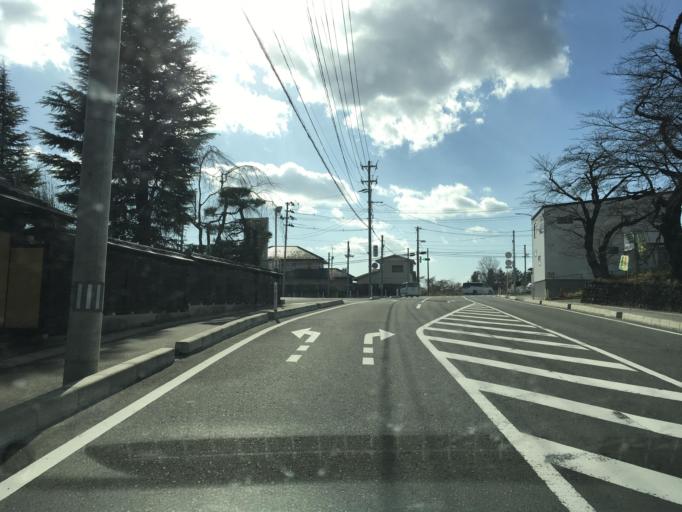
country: JP
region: Miyagi
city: Sendai
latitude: 38.2895
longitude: 140.7479
